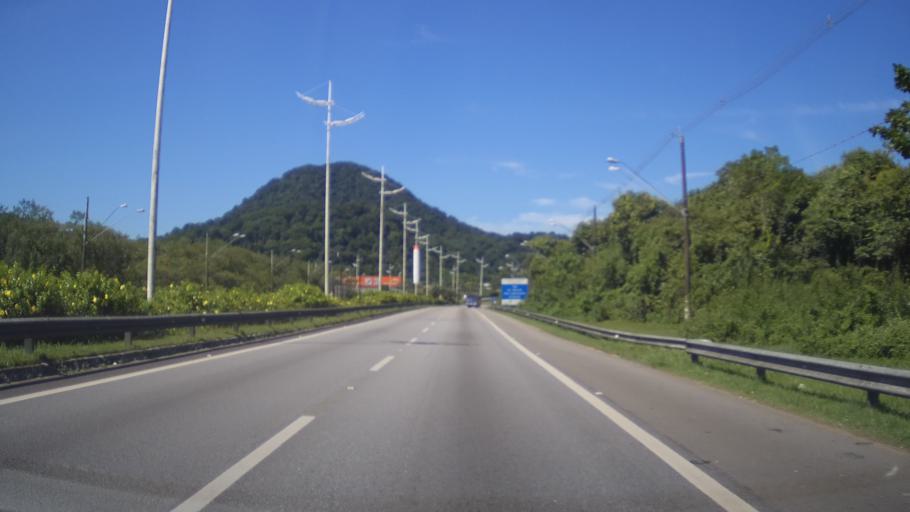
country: BR
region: Sao Paulo
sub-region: Praia Grande
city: Praia Grande
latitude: -23.9858
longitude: -46.4007
